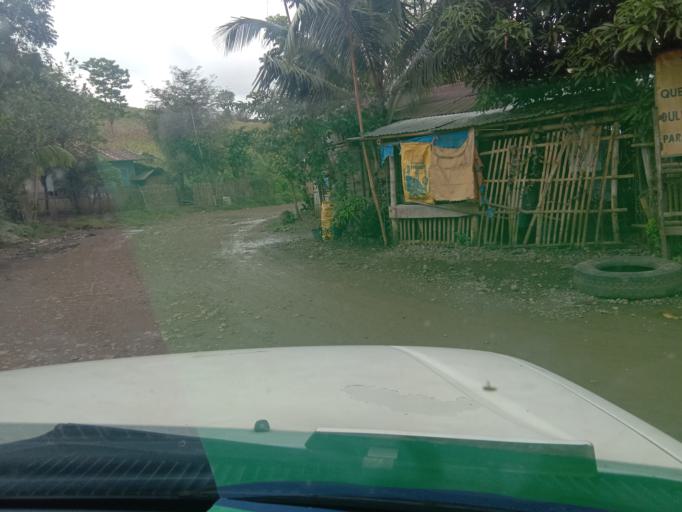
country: PH
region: Western Visayas
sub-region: Province of Capiz
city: Lantangan
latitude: 11.3707
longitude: 122.8831
